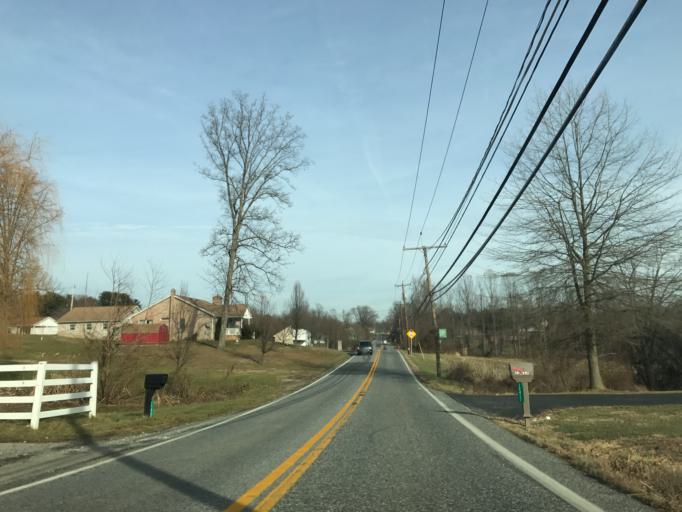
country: US
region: Maryland
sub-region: Baltimore County
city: Kingsville
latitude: 39.4648
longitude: -76.4478
